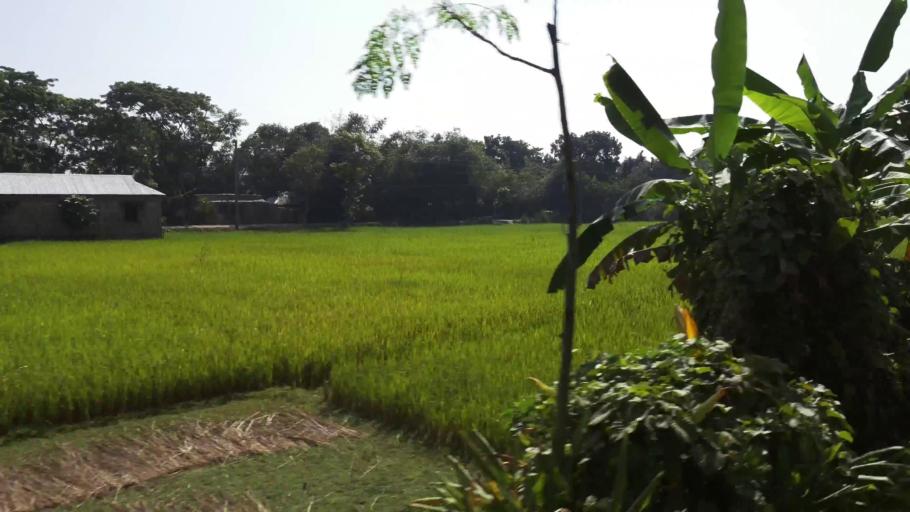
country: BD
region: Dhaka
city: Gafargaon
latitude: 24.5563
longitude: 90.5084
